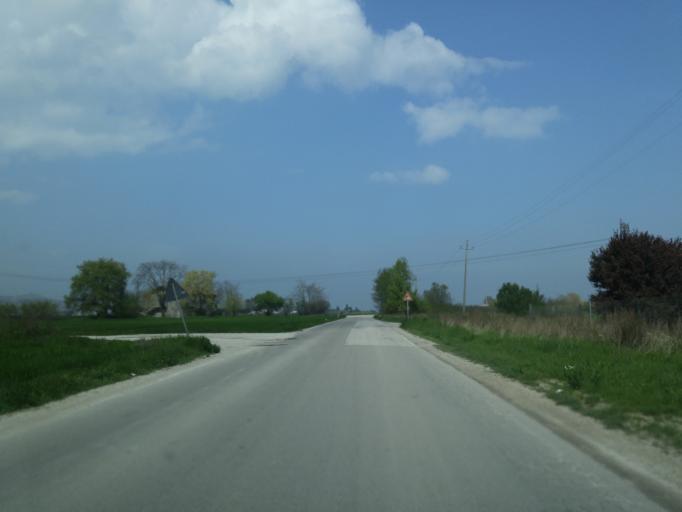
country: IT
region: The Marches
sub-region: Provincia di Pesaro e Urbino
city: Cuccurano
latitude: 43.7713
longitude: 12.9754
